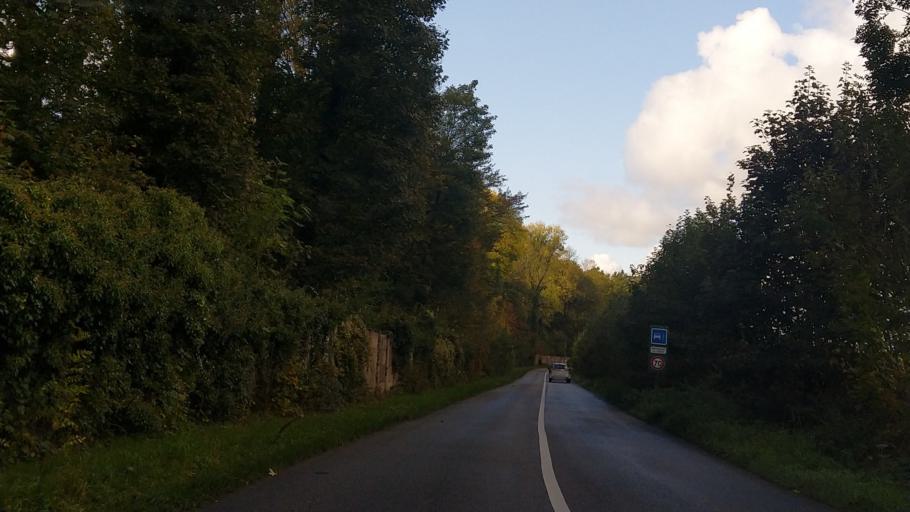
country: FR
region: Ile-de-France
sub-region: Departement du Val-d'Oise
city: Baillet-en-France
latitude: 49.0662
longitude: 2.2946
